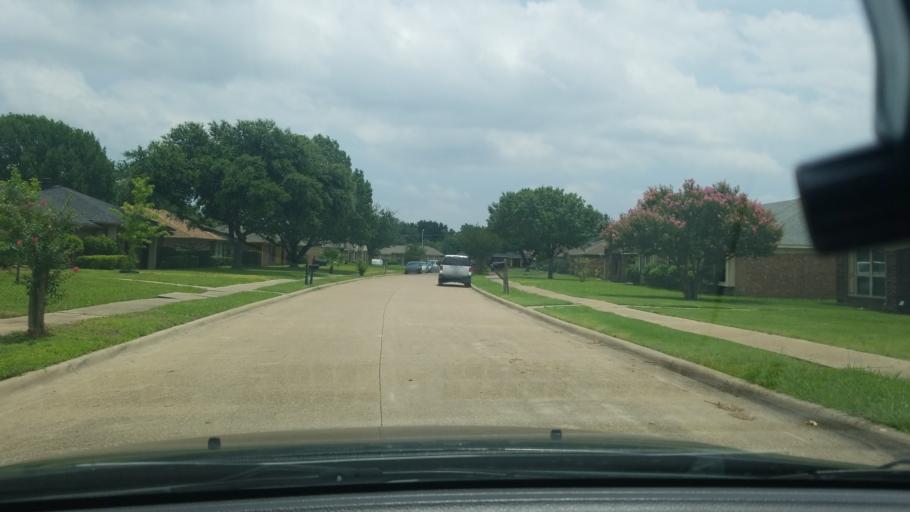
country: US
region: Texas
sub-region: Dallas County
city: Mesquite
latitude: 32.8009
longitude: -96.6190
